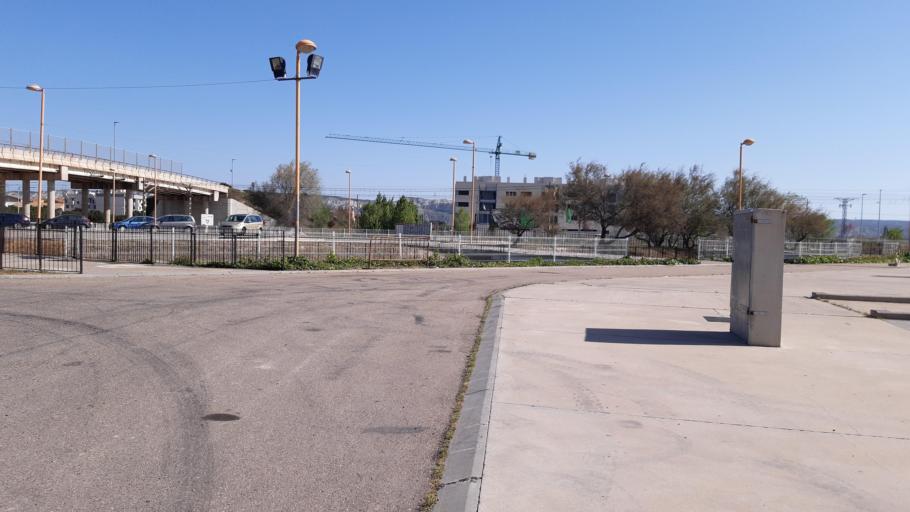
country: ES
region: Aragon
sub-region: Provincia de Zaragoza
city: Utebo
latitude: 41.7085
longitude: -0.9960
